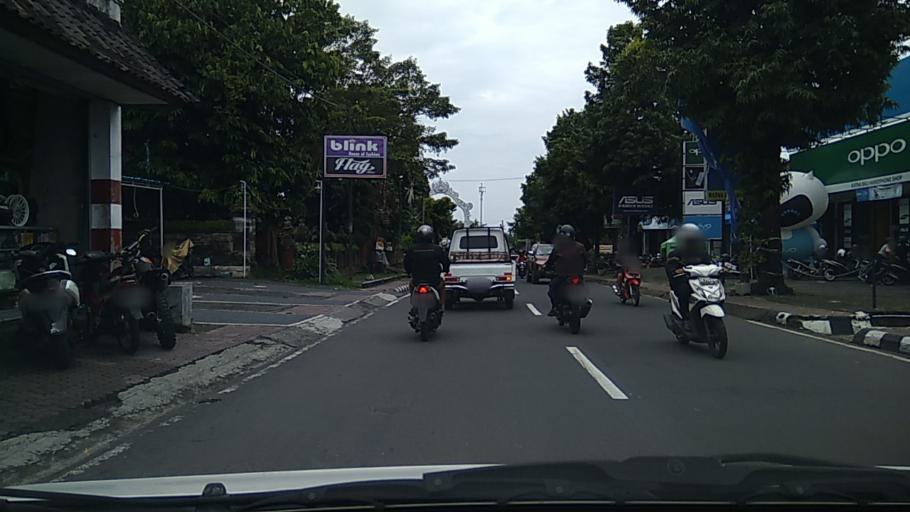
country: ID
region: Bali
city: Banjar Kelodan
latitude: -8.5419
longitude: 115.3316
